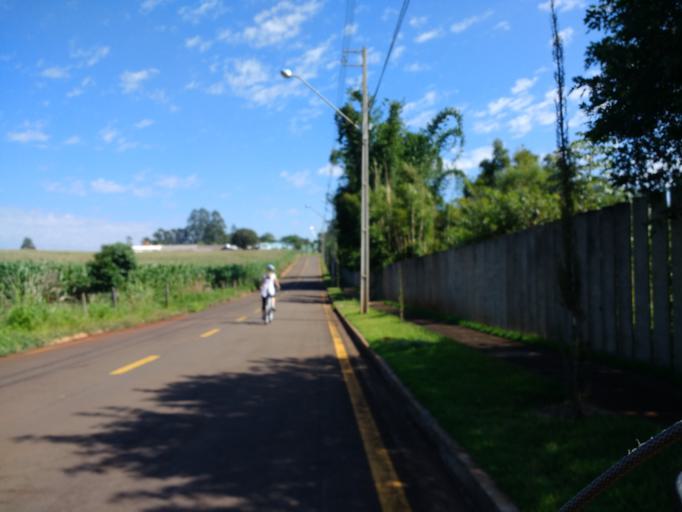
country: BR
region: Parana
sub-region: Londrina
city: Londrina
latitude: -23.3667
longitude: -51.1925
